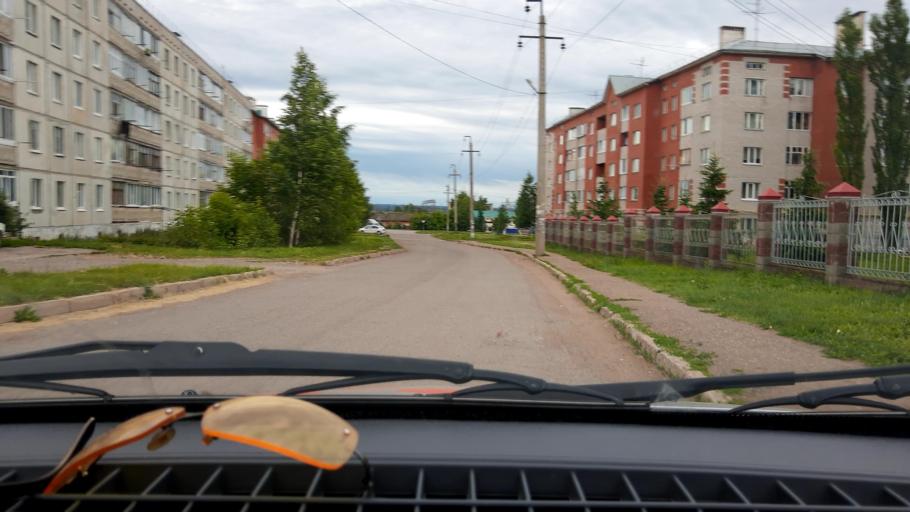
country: RU
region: Bashkortostan
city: Chishmy
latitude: 54.5911
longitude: 55.3963
